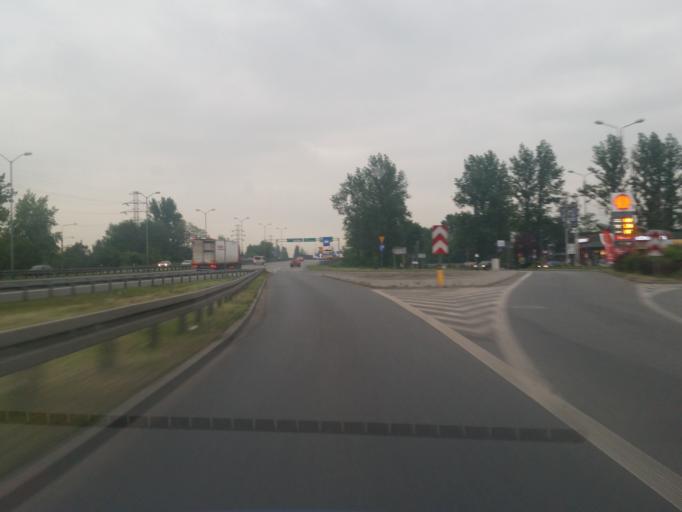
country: PL
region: Silesian Voivodeship
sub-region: Katowice
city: Katowice
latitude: 50.2714
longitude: 19.0648
